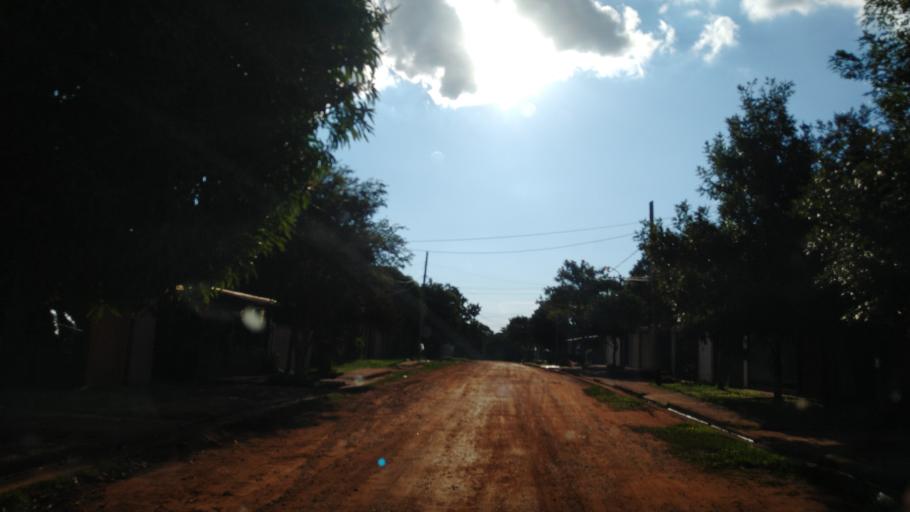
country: AR
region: Misiones
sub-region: Departamento de Capital
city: Posadas
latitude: -27.4060
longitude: -55.9296
